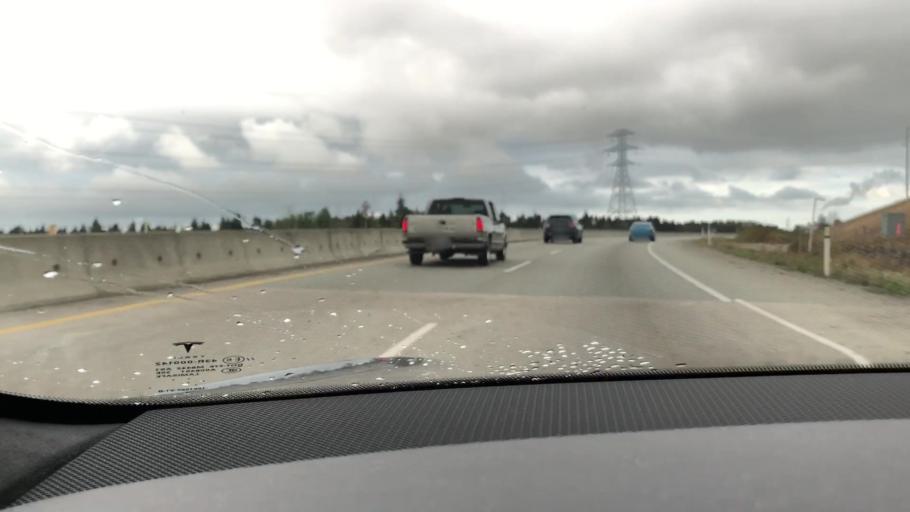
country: CA
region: British Columbia
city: Delta
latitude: 49.1470
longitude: -122.9710
